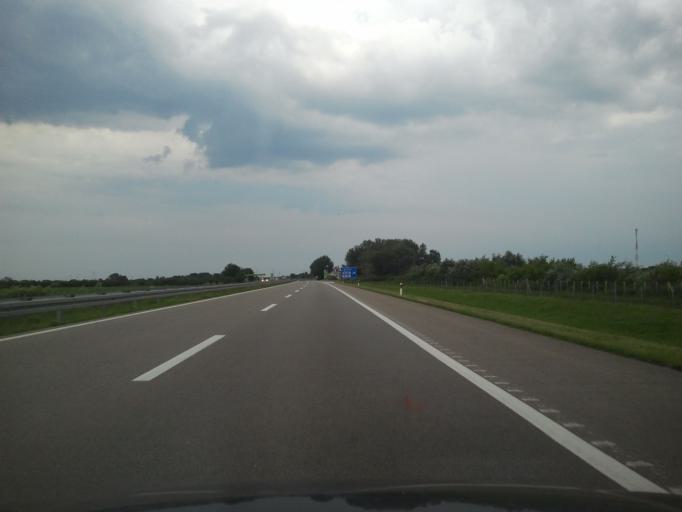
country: RS
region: Autonomna Pokrajina Vojvodina
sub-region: Sremski Okrug
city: Sremska Mitrovica
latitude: 45.0029
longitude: 19.6168
